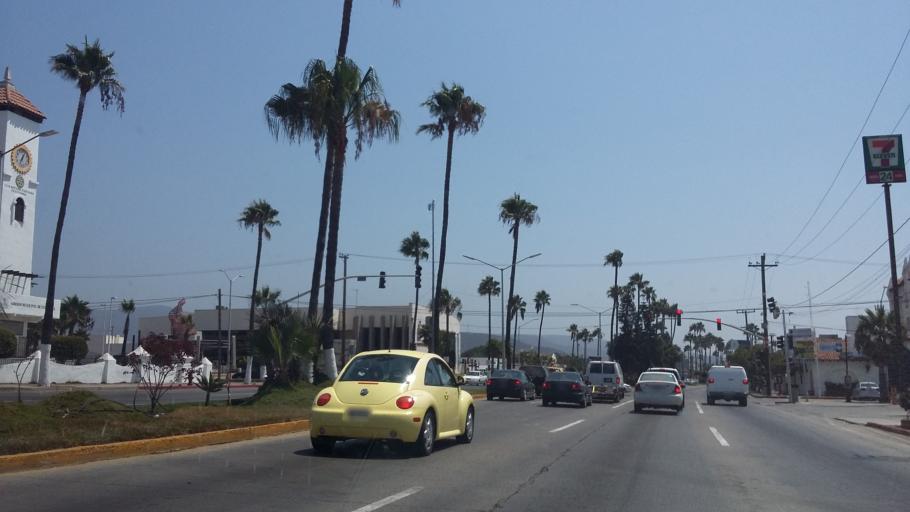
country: MX
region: Baja California
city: Ensenada
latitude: 31.8574
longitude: -116.6195
